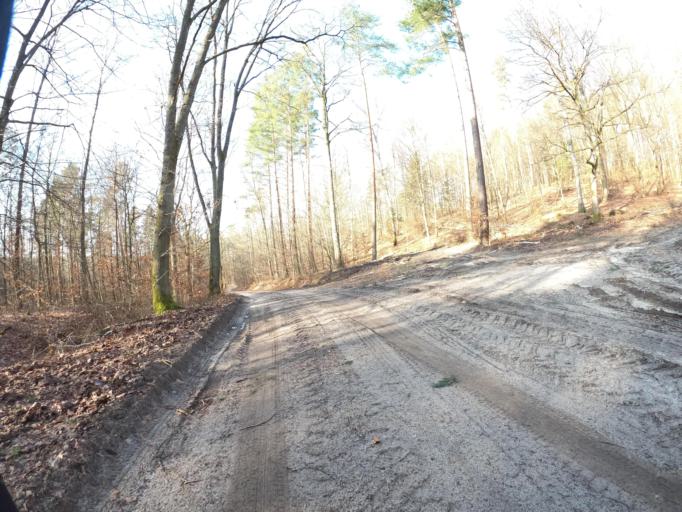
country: PL
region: West Pomeranian Voivodeship
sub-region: Powiat koszalinski
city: Polanow
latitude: 54.2367
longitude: 16.6719
